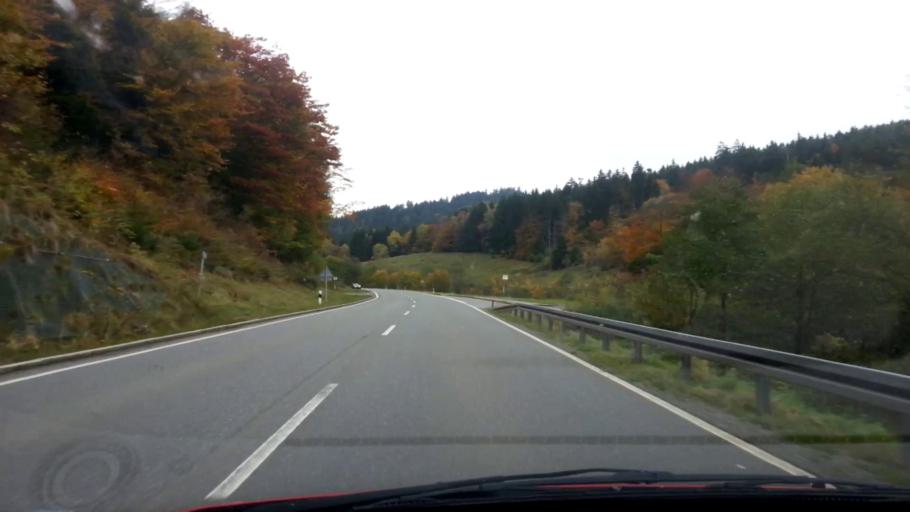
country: DE
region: Bavaria
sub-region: Upper Franconia
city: Warmensteinach
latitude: 49.9688
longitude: 11.7659
